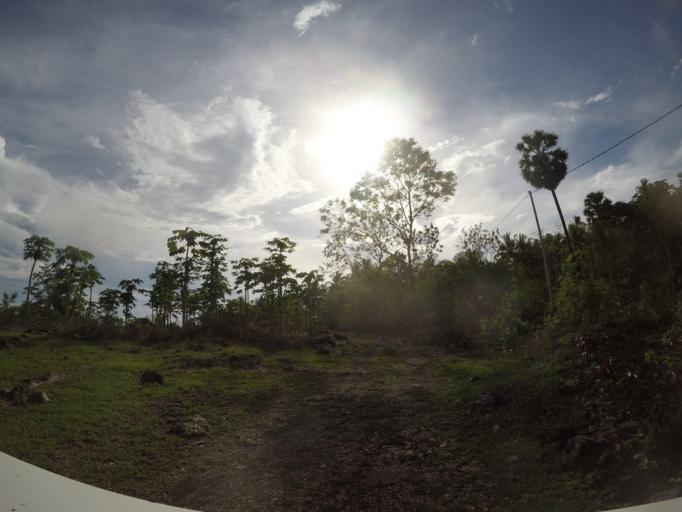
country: TL
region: Baucau
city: Baucau
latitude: -8.5013
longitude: 126.4542
